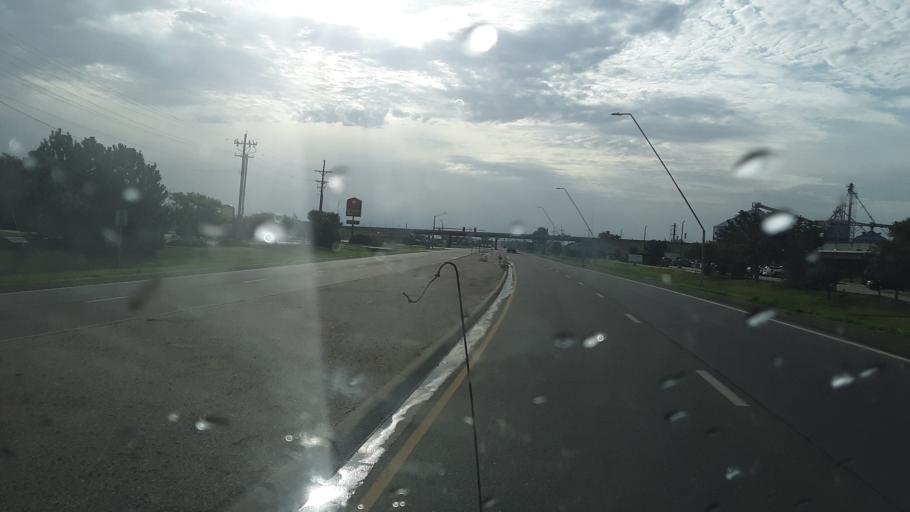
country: US
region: Kansas
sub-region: Finney County
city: Garden City
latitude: 37.9604
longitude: -100.8434
